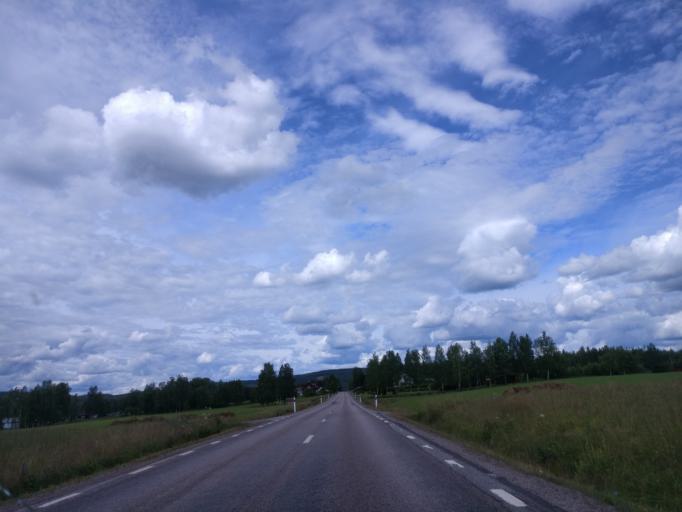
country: SE
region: Vaermland
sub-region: Hagfors Kommun
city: Ekshaerad
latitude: 60.1589
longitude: 13.4193
